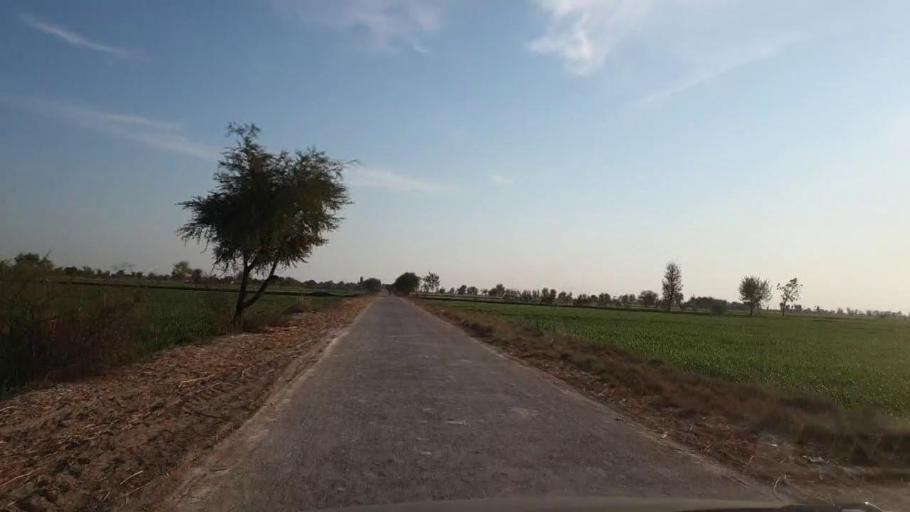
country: PK
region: Sindh
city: Khadro
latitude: 26.1977
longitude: 68.7470
